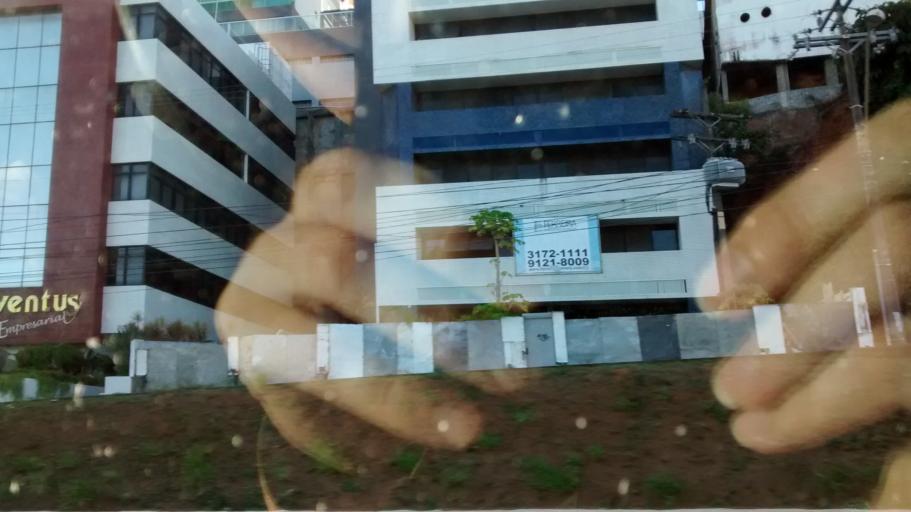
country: BR
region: Bahia
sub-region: Salvador
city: Salvador
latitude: -13.0065
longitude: -38.4905
